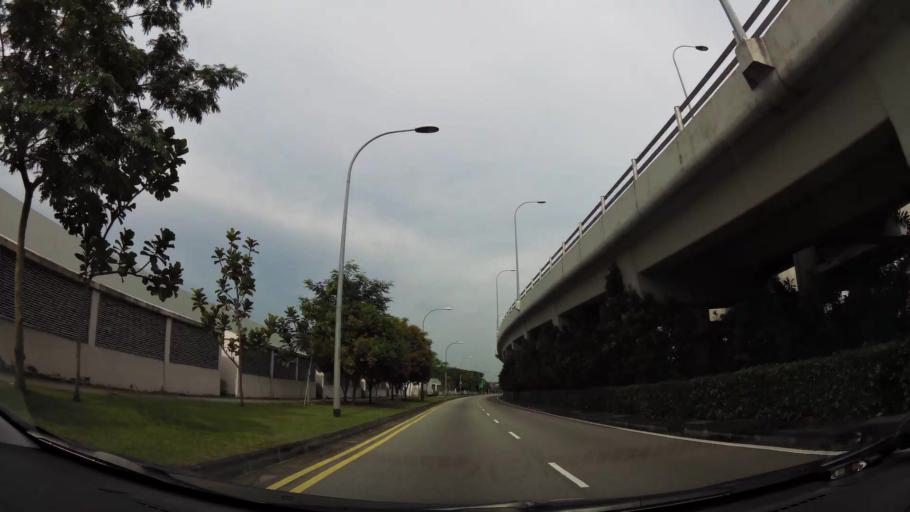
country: SG
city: Singapore
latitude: 1.3425
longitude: 103.8886
